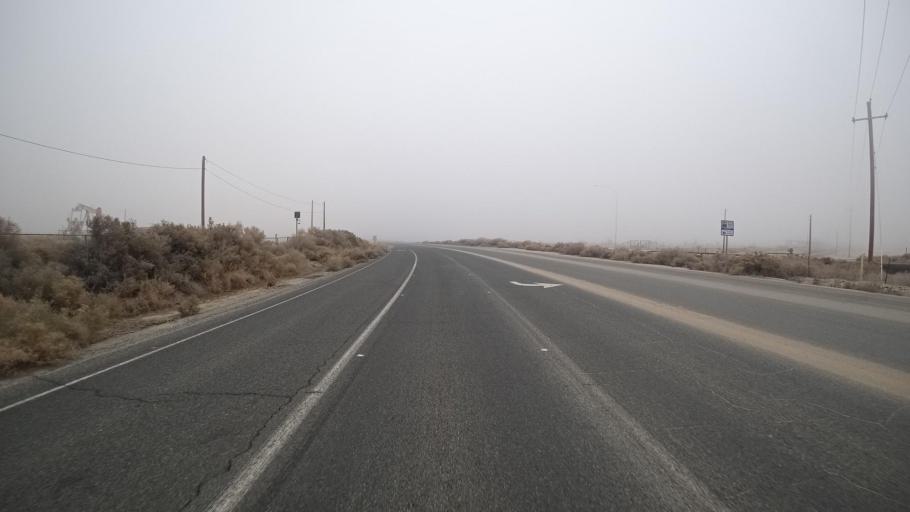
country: US
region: California
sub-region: Kern County
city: Buttonwillow
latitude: 35.2776
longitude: -119.4676
